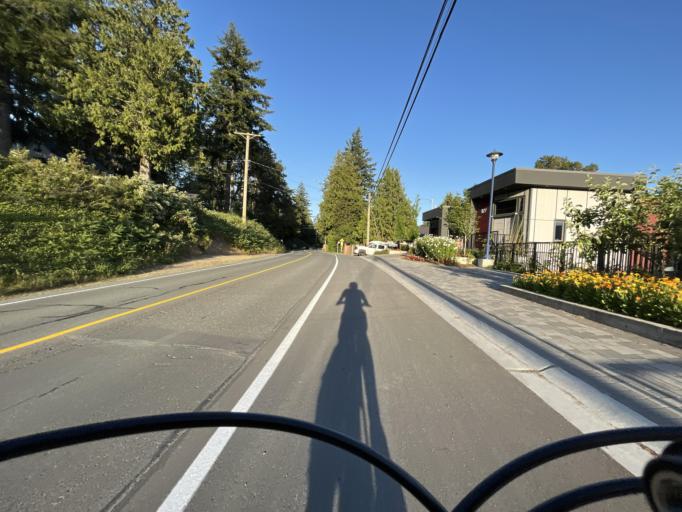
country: CA
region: British Columbia
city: Langford
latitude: 48.4498
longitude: -123.5250
